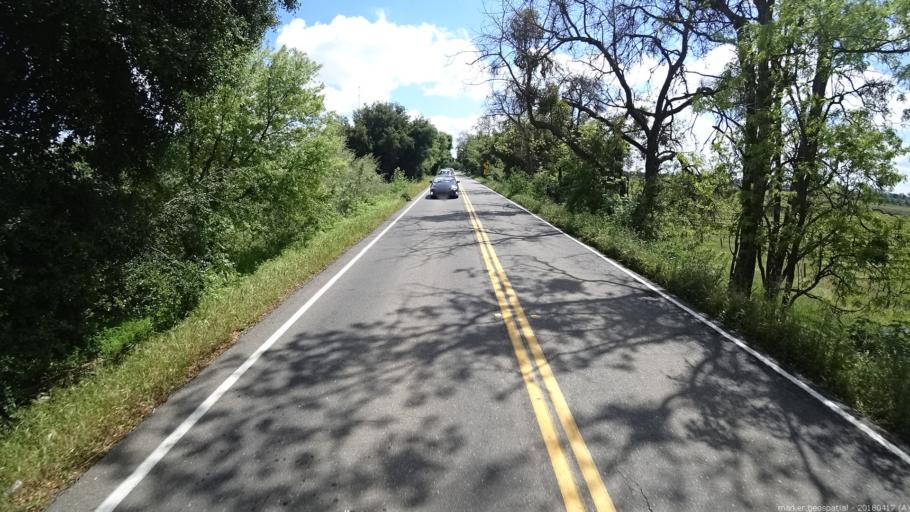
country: US
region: California
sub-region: Sacramento County
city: Walnut Grove
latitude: 38.2377
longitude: -121.5326
